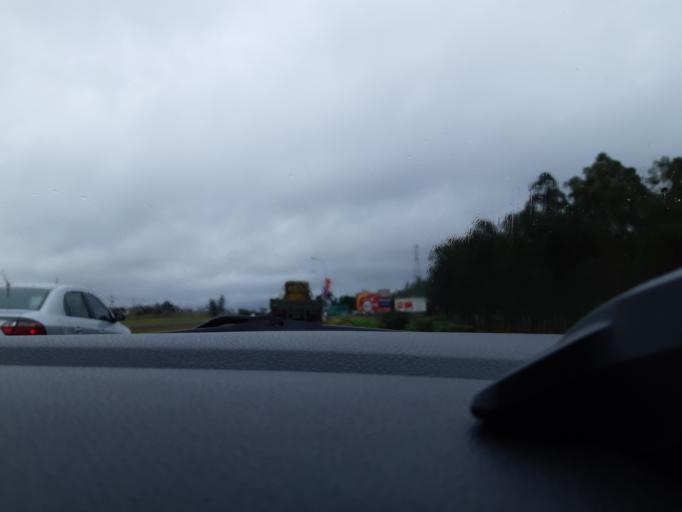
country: BR
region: Sao Paulo
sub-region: Ourinhos
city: Ourinhos
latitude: -22.9855
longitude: -49.9036
